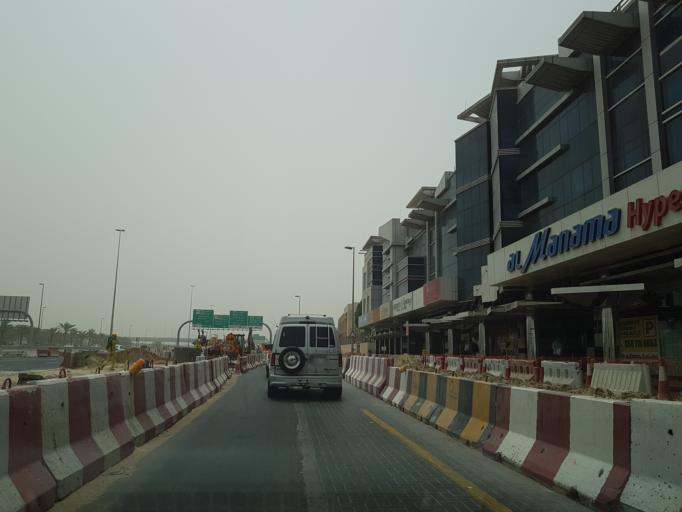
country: AE
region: Dubai
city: Dubai
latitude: 25.1730
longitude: 55.2595
